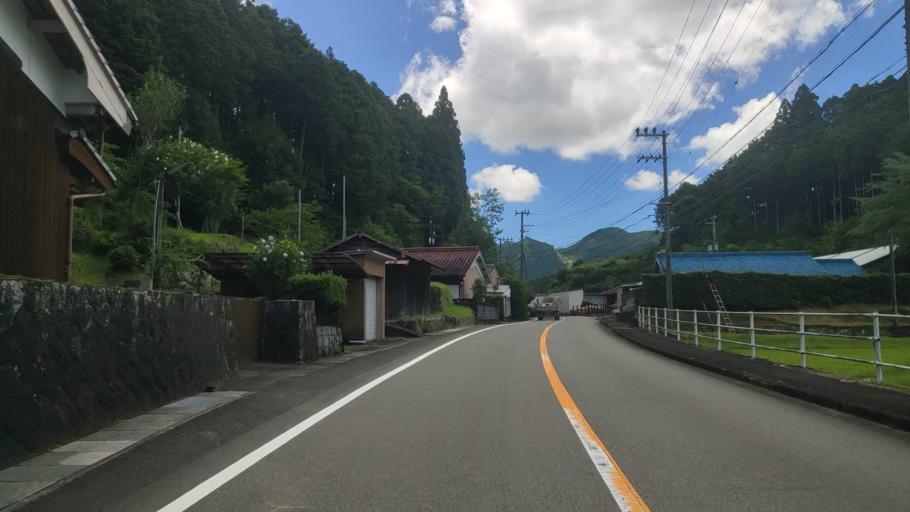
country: JP
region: Mie
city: Owase
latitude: 33.9512
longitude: 136.0693
